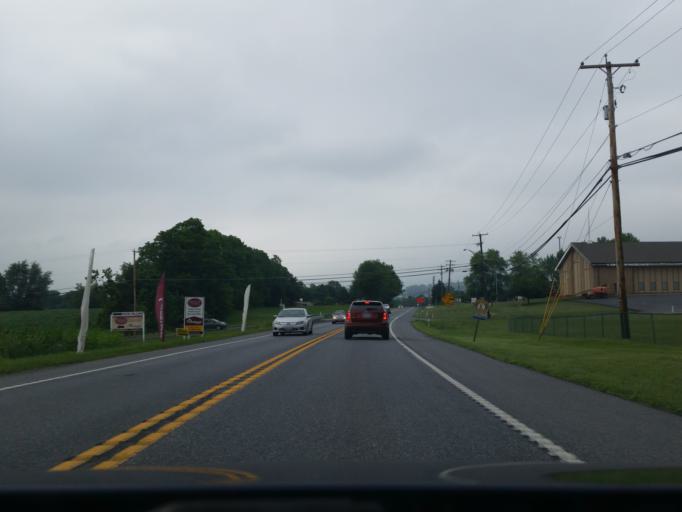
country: US
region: Pennsylvania
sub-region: Lebanon County
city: Annville
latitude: 40.3183
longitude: -76.5082
